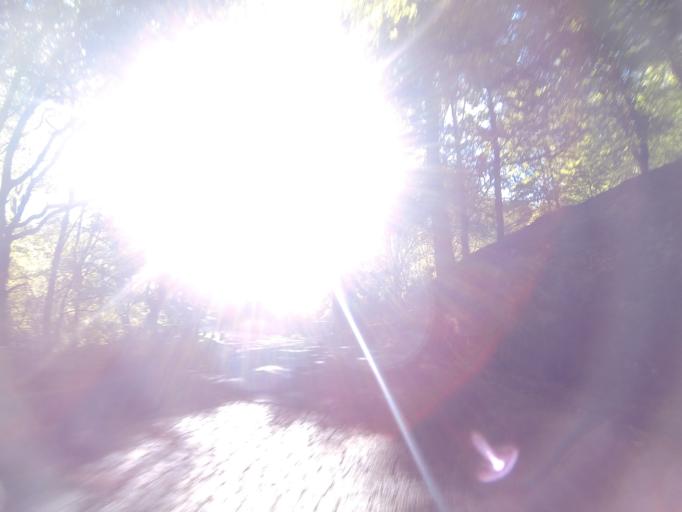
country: PT
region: Madeira
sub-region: Funchal
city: Nossa Senhora do Monte
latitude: 32.6986
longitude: -16.8837
